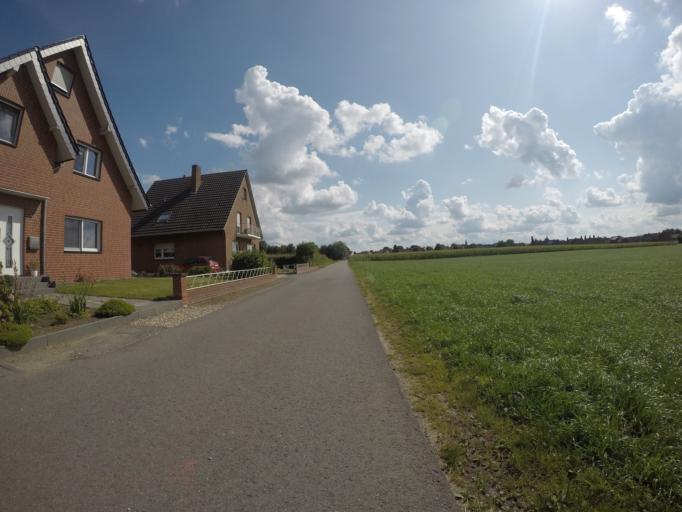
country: DE
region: North Rhine-Westphalia
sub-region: Regierungsbezirk Dusseldorf
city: Hamminkeln
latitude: 51.7370
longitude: 6.5848
